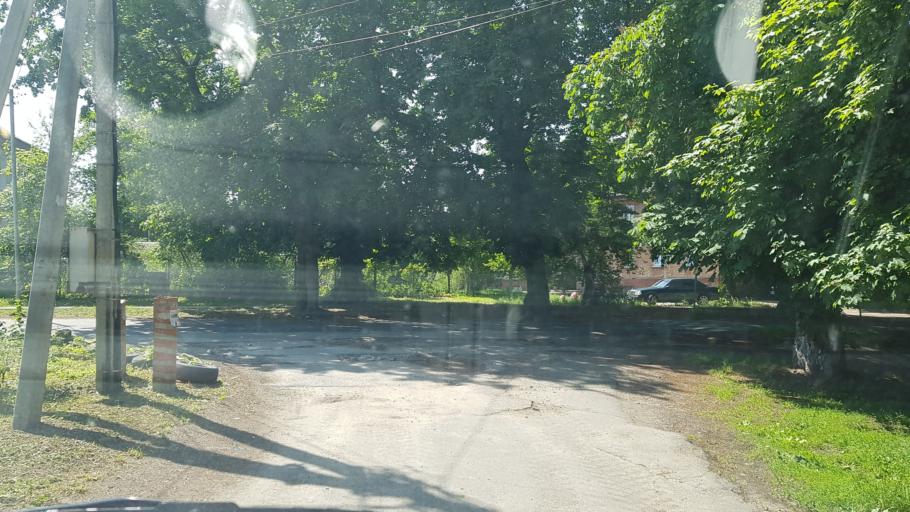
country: RU
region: Kaliningrad
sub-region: Gorod Kaliningrad
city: Baltiysk
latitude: 54.6463
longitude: 19.8877
